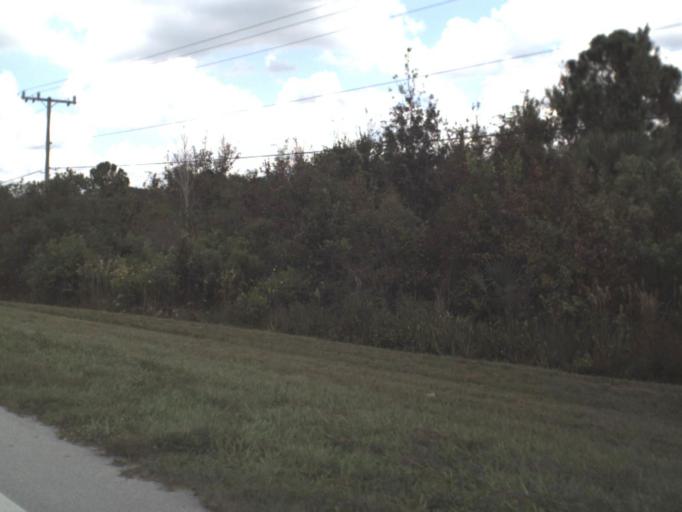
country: US
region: Florida
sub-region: Okeechobee County
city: Okeechobee
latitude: 27.2685
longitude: -80.8674
